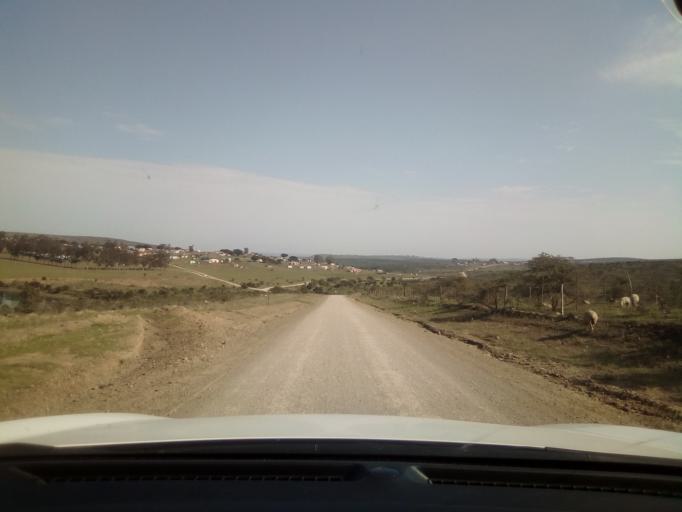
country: ZA
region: Eastern Cape
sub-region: Buffalo City Metropolitan Municipality
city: Bhisho
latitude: -32.9879
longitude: 27.2447
